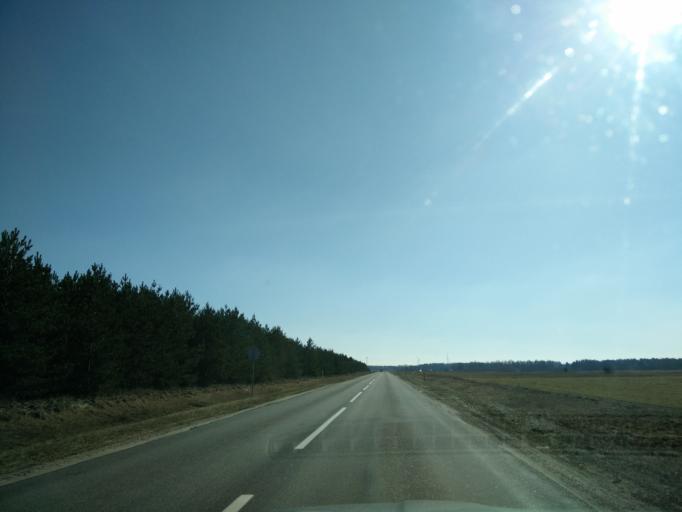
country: LT
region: Klaipedos apskritis
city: Silute
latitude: 55.3252
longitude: 21.5251
